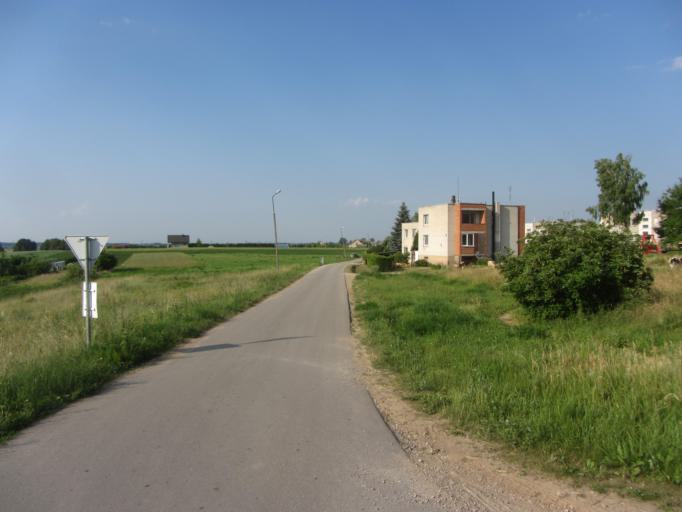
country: LT
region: Alytaus apskritis
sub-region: Alytus
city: Alytus
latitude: 54.3985
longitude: 23.9272
